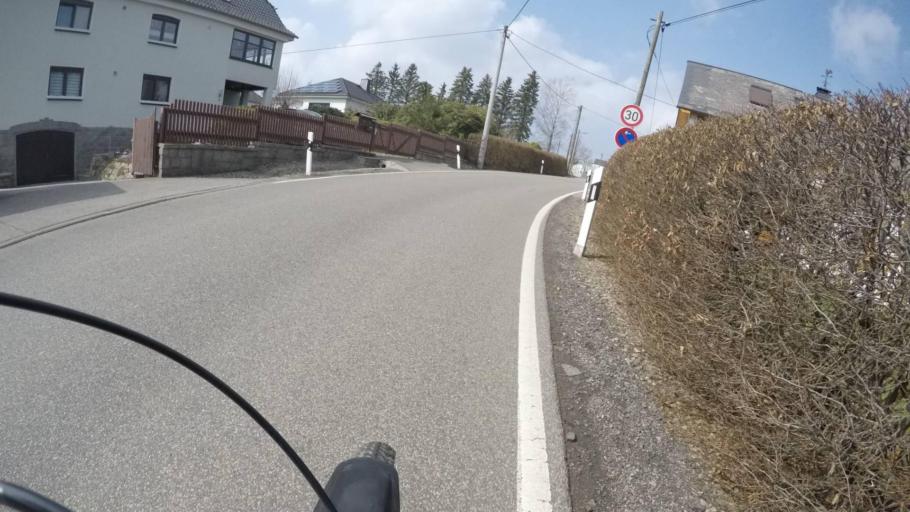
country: DE
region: Saxony
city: Limbach-Oberfrohna
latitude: 50.8302
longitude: 12.7399
